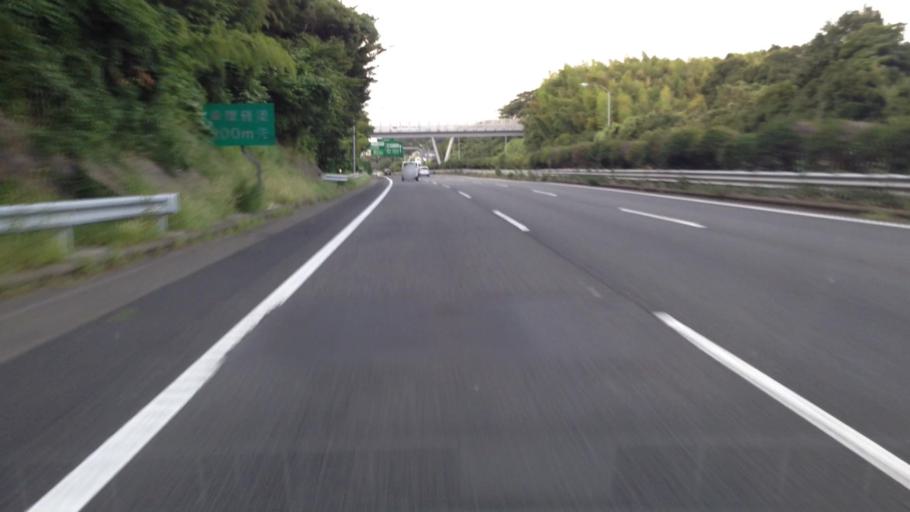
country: JP
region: Kanagawa
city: Yokohama
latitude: 35.5046
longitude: 139.5925
